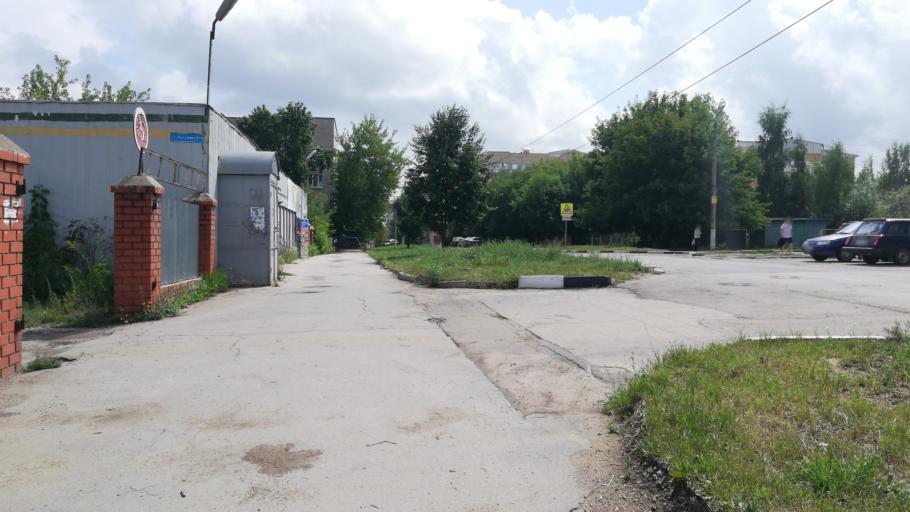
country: RU
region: Tula
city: Tula
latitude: 54.1992
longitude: 37.6409
